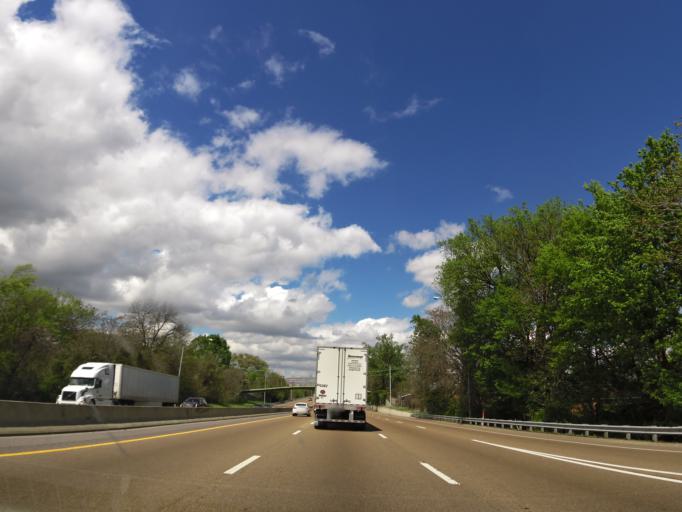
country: US
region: Tennessee
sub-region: Shelby County
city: Memphis
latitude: 35.1762
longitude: -90.0182
